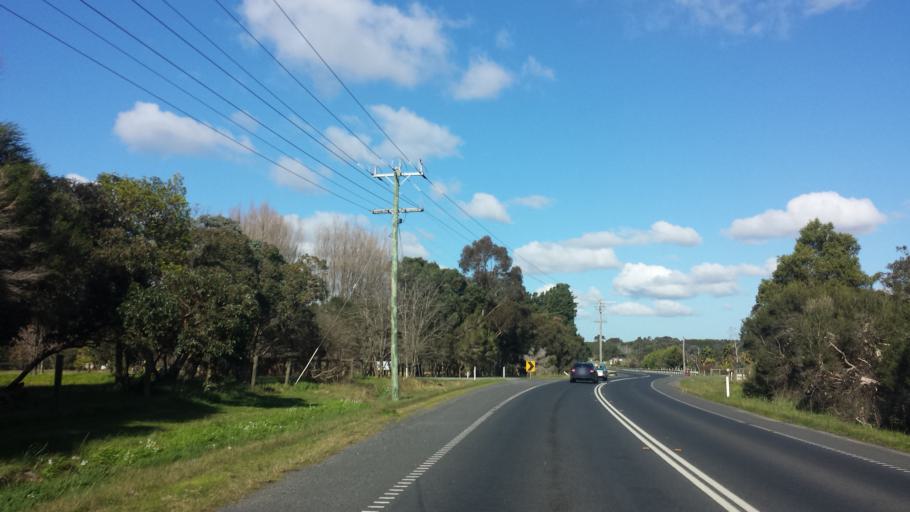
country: AU
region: Victoria
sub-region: Casey
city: Narre Warren North
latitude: -37.9701
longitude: 145.3164
